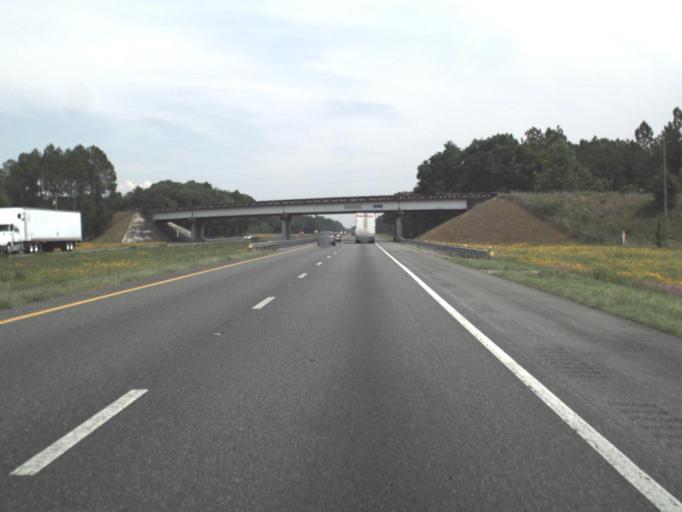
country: US
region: Florida
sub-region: Suwannee County
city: Live Oak
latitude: 30.3128
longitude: -82.9355
